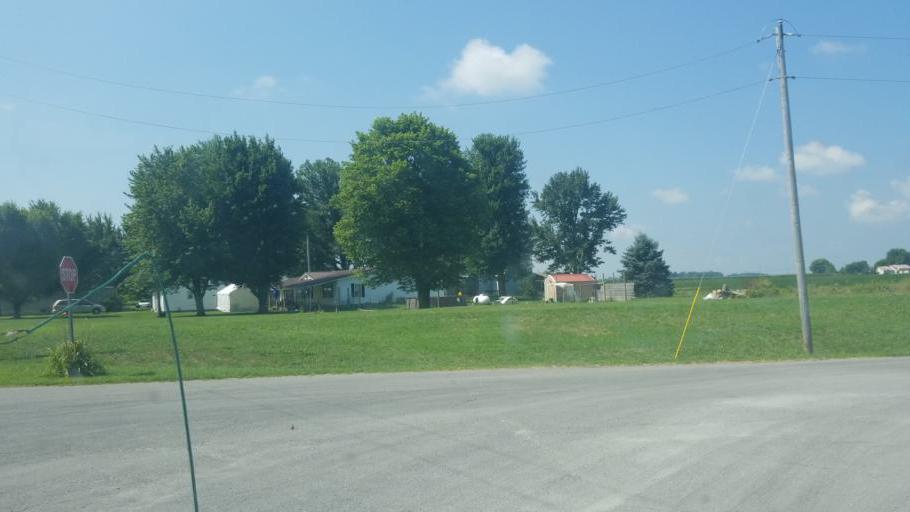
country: US
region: Ohio
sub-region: Hardin County
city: Kenton
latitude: 40.6767
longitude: -83.7293
